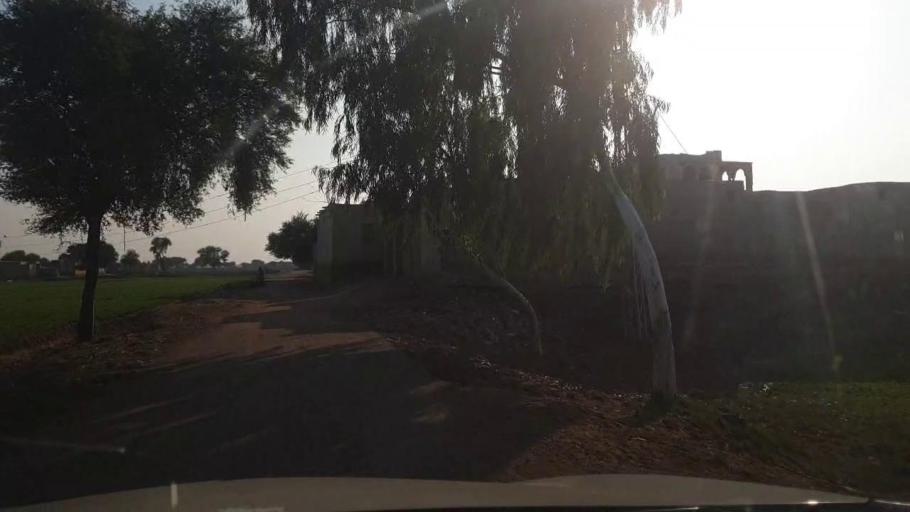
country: PK
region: Sindh
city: Bhan
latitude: 26.4649
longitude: 67.7216
